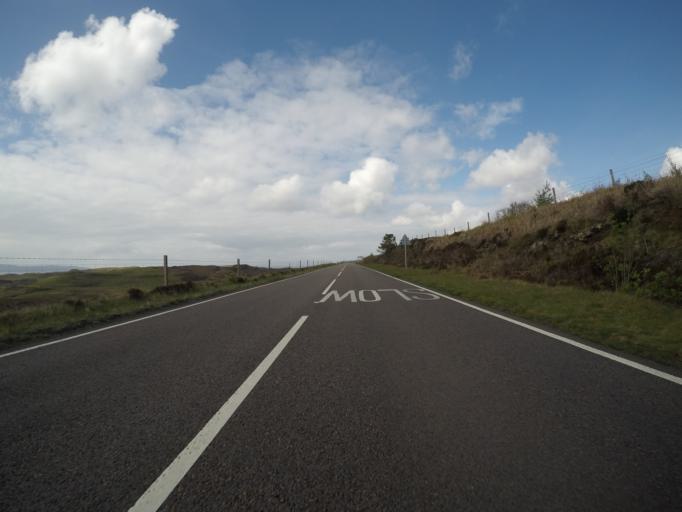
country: GB
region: Scotland
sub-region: Highland
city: Portree
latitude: 57.5503
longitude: -6.3643
